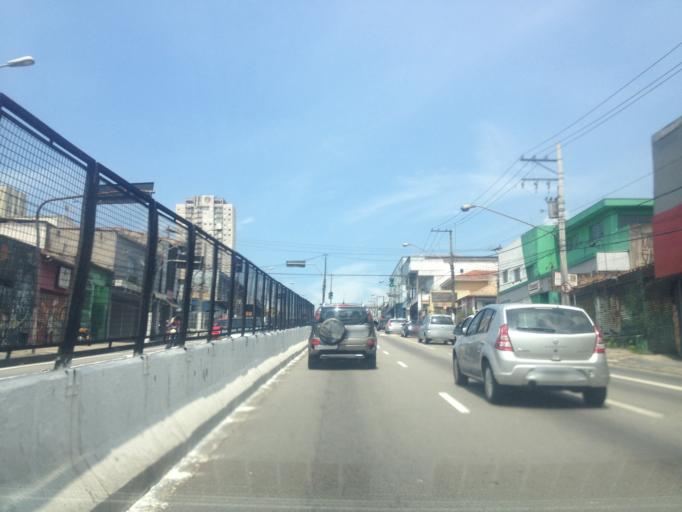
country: BR
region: Sao Paulo
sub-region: Diadema
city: Diadema
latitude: -23.6371
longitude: -46.6710
